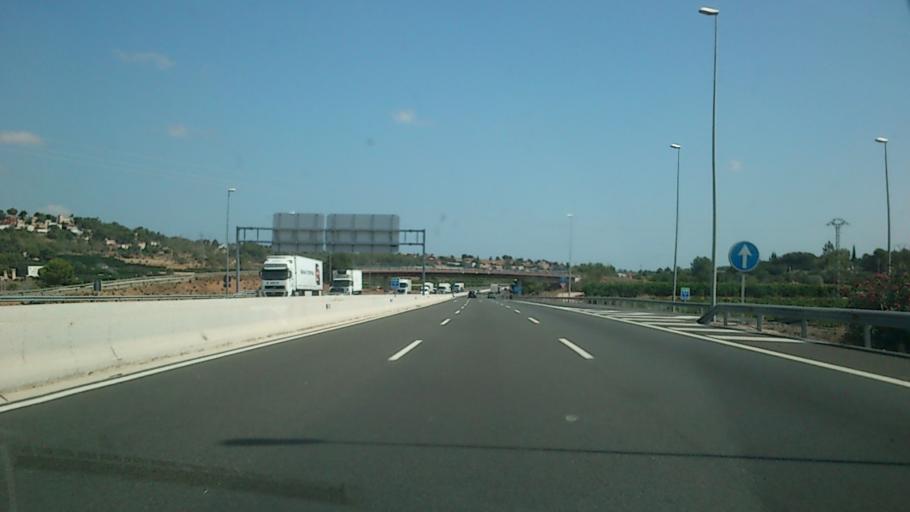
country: ES
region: Valencia
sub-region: Provincia de Valencia
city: Torrent
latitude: 39.4162
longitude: -0.5082
